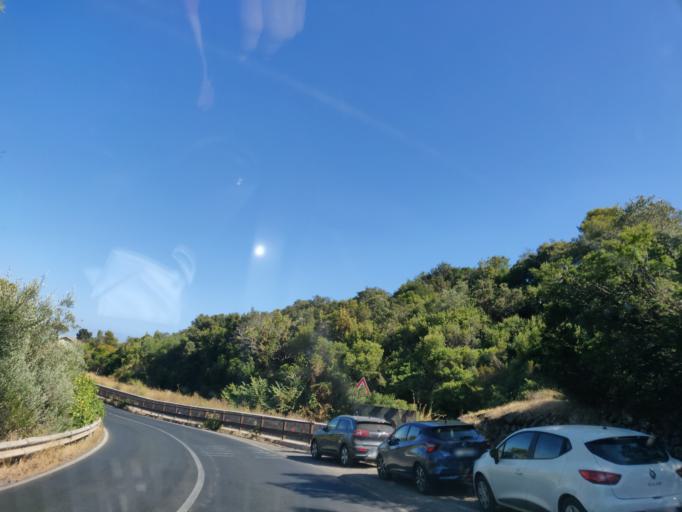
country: IT
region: Tuscany
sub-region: Provincia di Grosseto
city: Monte Argentario
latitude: 42.4349
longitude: 11.1518
